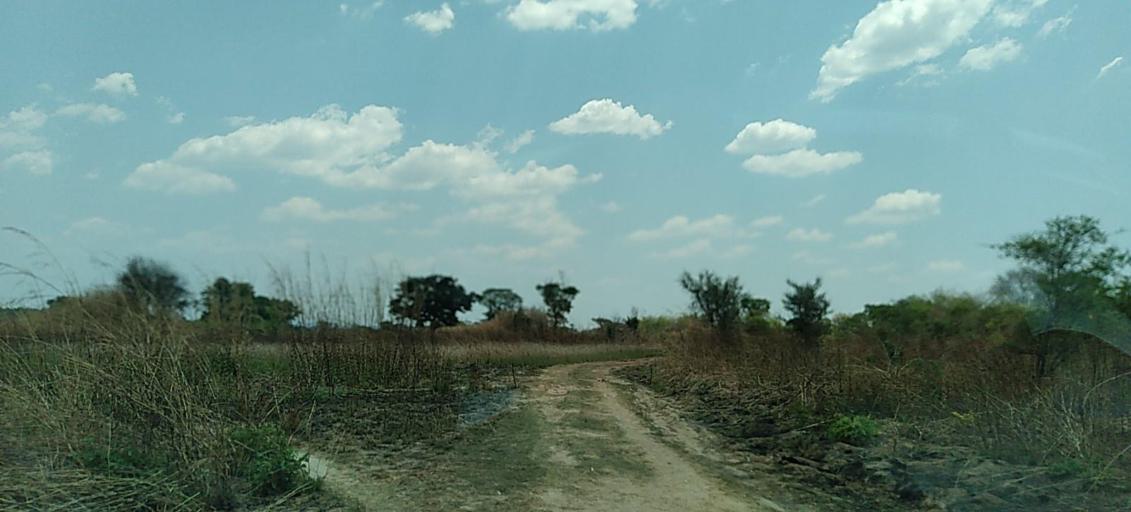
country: ZM
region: Copperbelt
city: Chililabombwe
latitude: -12.4681
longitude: 27.6660
